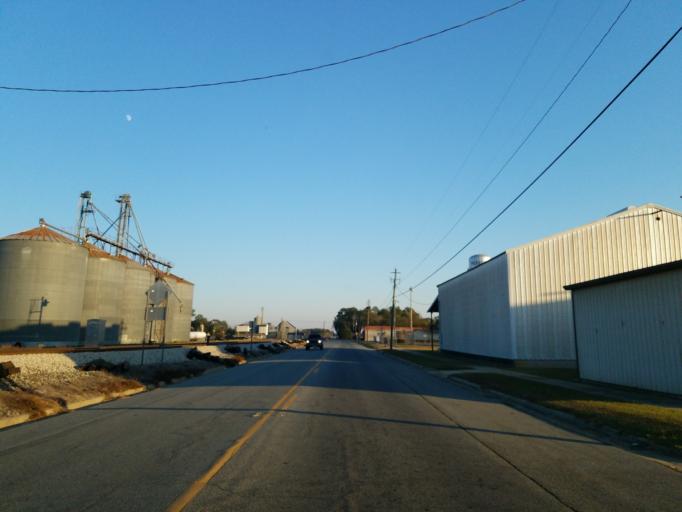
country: US
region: Georgia
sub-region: Wilcox County
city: Rochelle
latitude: 31.8085
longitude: -83.4893
